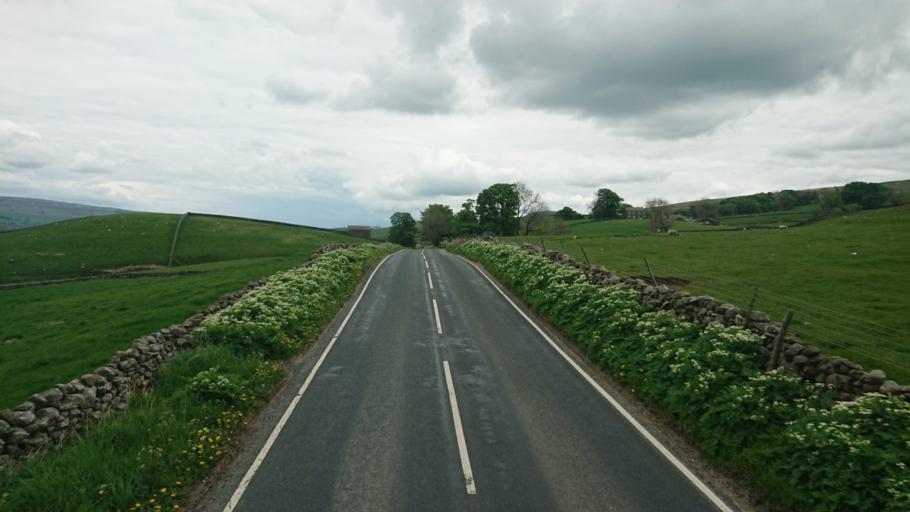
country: GB
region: England
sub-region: County Durham
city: Bowes
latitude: 54.3025
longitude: -2.1552
